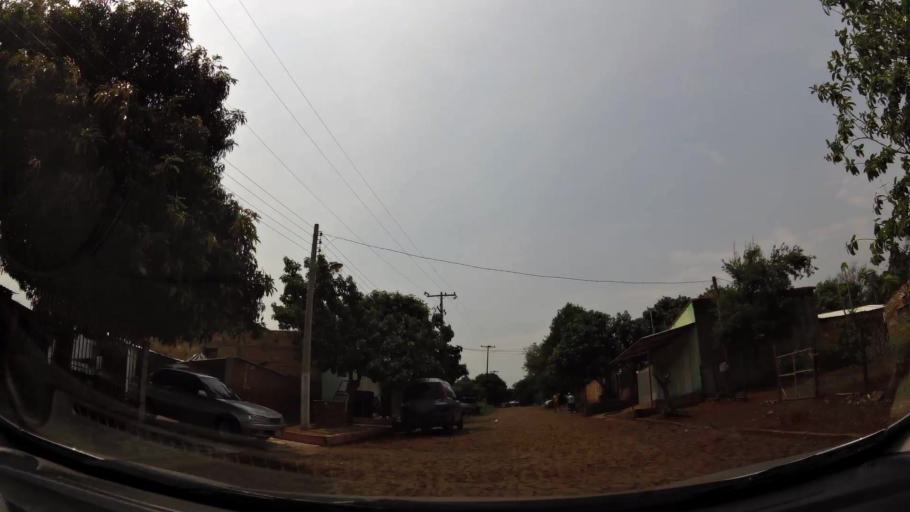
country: PY
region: Alto Parana
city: Presidente Franco
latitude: -25.5687
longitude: -54.6174
